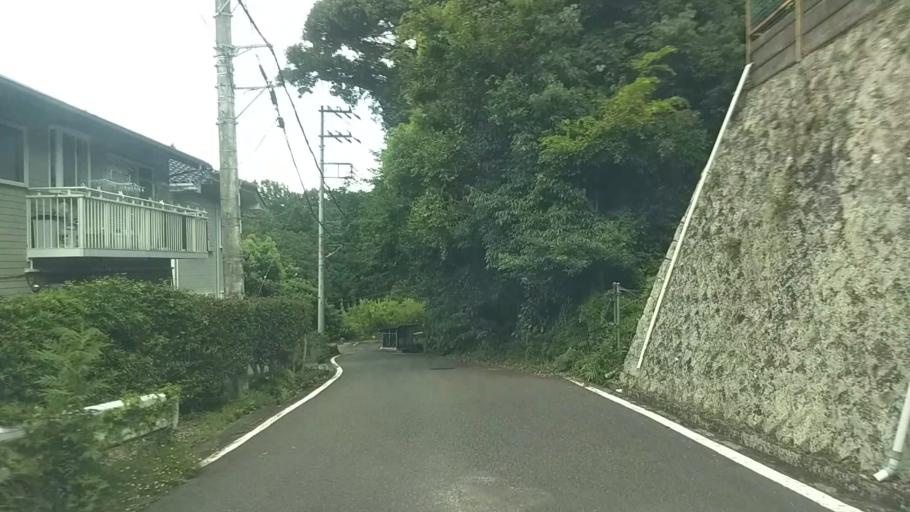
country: JP
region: Shizuoka
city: Mishima
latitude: 34.9977
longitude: 138.9441
